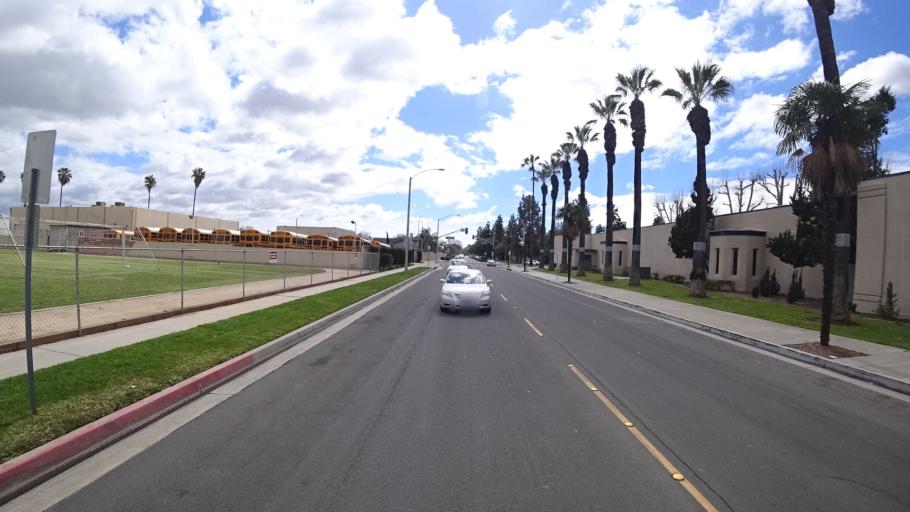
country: US
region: California
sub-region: Orange County
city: Anaheim
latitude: 33.8297
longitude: -117.9371
